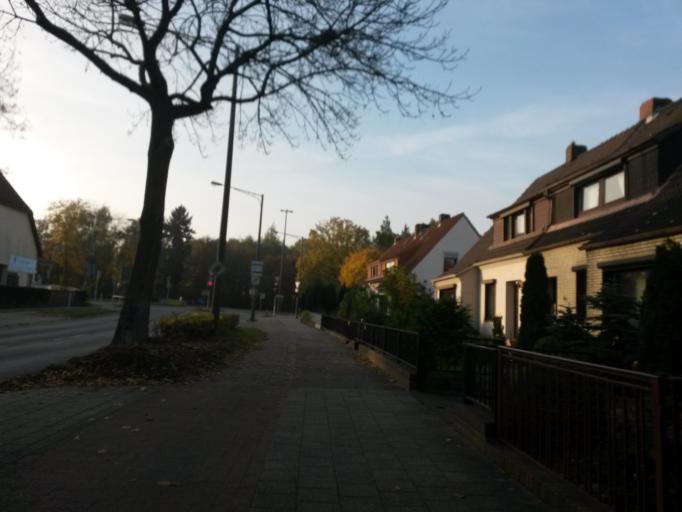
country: DE
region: Bremen
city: Bremen
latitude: 53.0315
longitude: 8.8104
